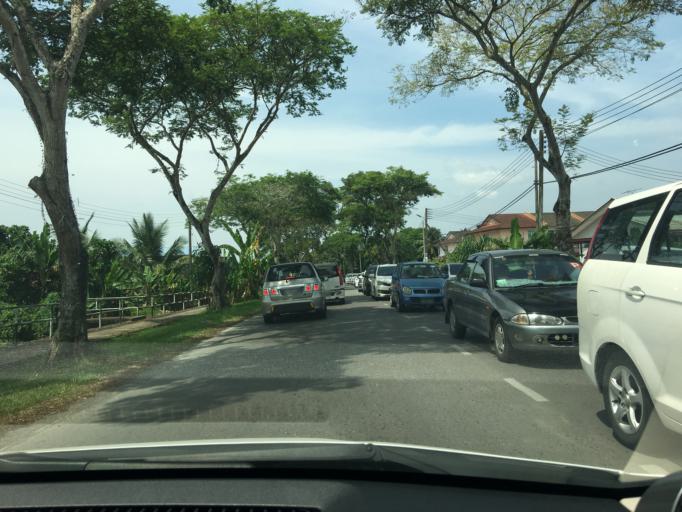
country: MY
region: Sarawak
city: Kuching
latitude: 1.5087
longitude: 110.3022
